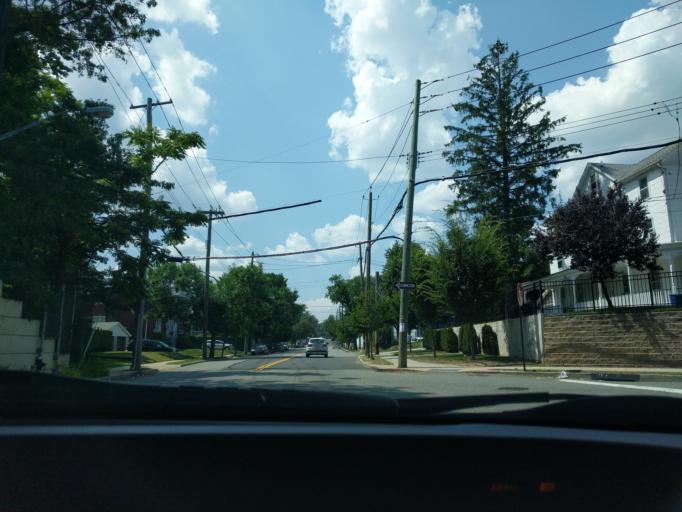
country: US
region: New York
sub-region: Richmond County
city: Staten Island
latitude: 40.5419
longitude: -74.1710
